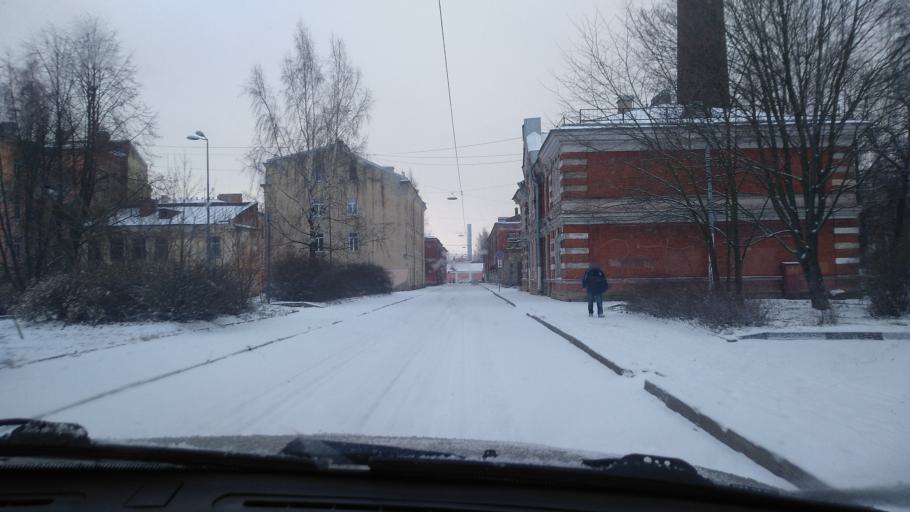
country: RU
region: St.-Petersburg
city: Kronshtadt
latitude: 59.9878
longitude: 29.7845
